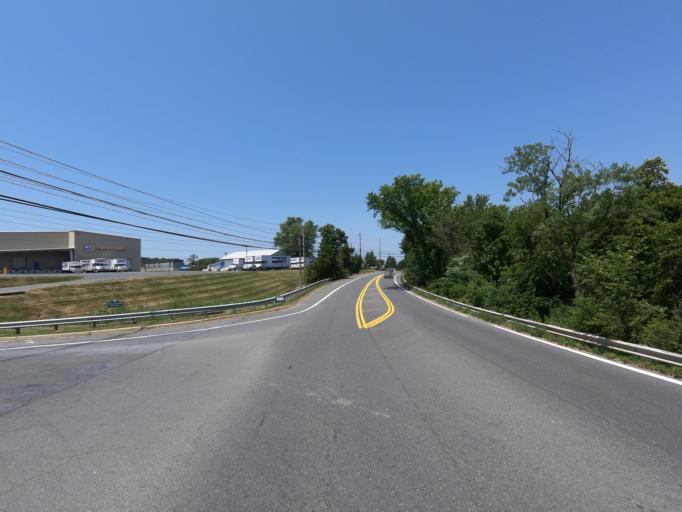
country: US
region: Maryland
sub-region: Montgomery County
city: Clarksburg
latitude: 39.2476
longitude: -77.2960
